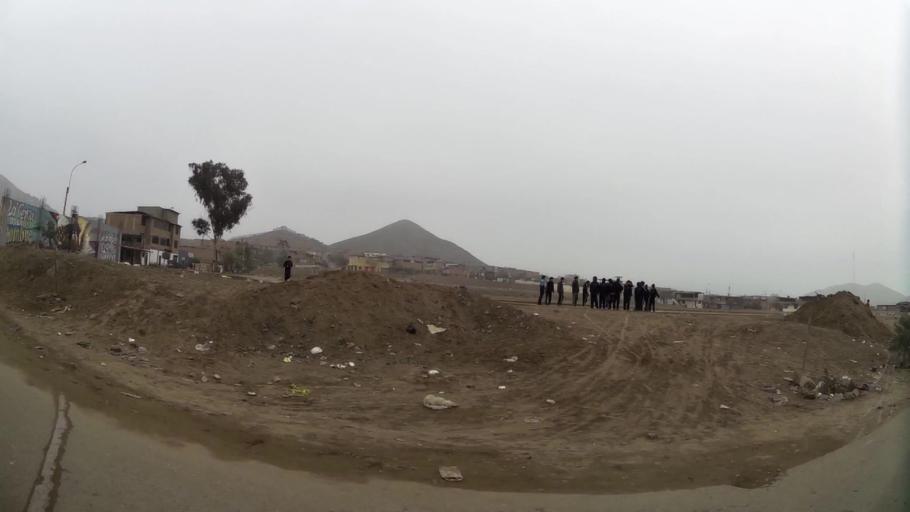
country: PE
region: Lima
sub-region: Lima
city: Surco
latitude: -12.1840
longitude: -76.9269
